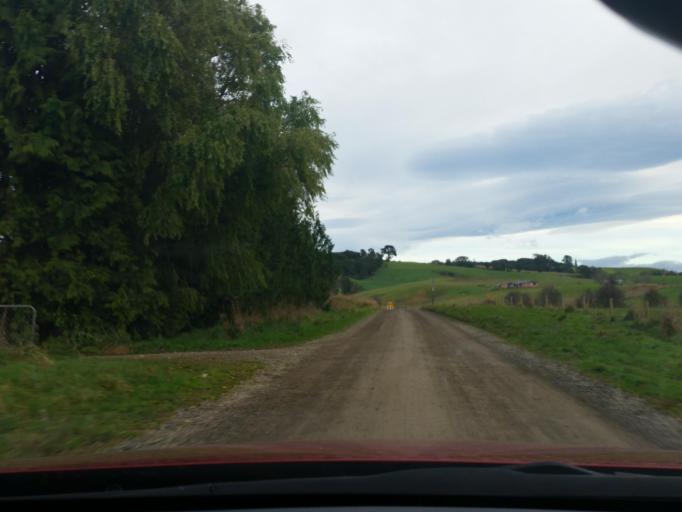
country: NZ
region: Southland
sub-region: Southland District
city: Riverton
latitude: -46.0997
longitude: 167.9414
